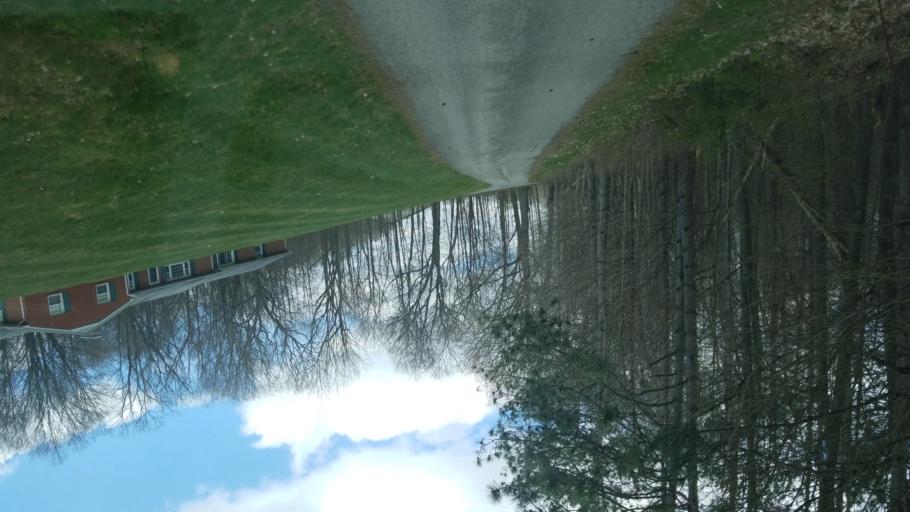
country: US
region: Ohio
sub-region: Knox County
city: Mount Vernon
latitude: 40.4409
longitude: -82.4441
